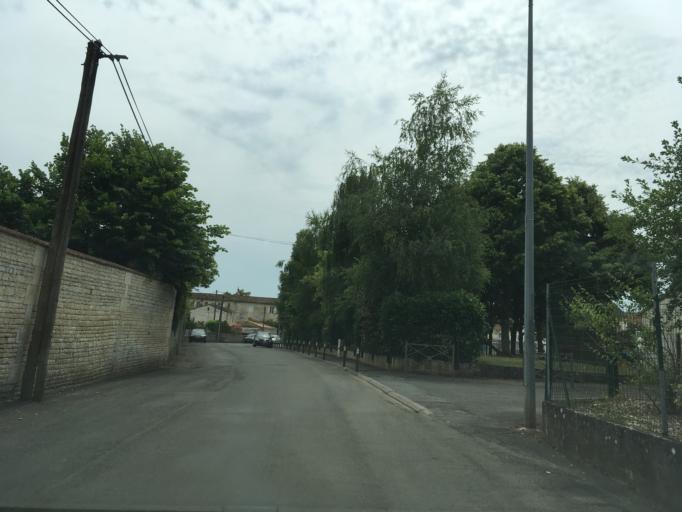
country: FR
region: Poitou-Charentes
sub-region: Departement des Deux-Sevres
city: Bessines
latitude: 46.3269
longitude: -0.5106
